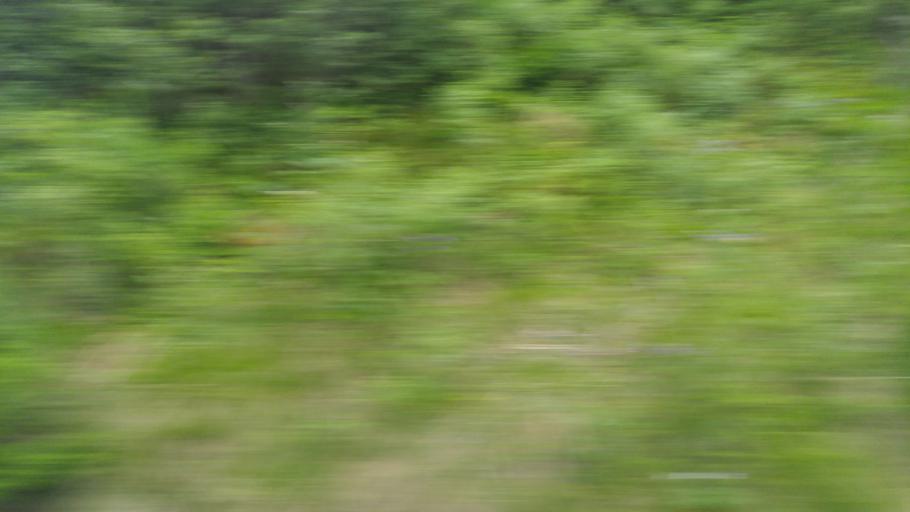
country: NO
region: Nord-Trondelag
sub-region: Levanger
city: Skogn
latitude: 63.4572
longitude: 11.3002
